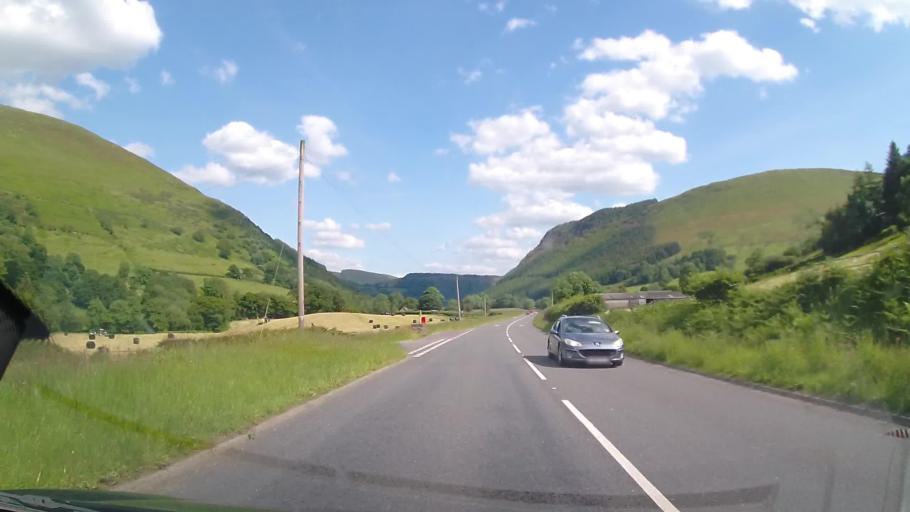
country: GB
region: Wales
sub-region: Gwynedd
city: Corris
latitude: 52.7310
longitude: -3.7175
